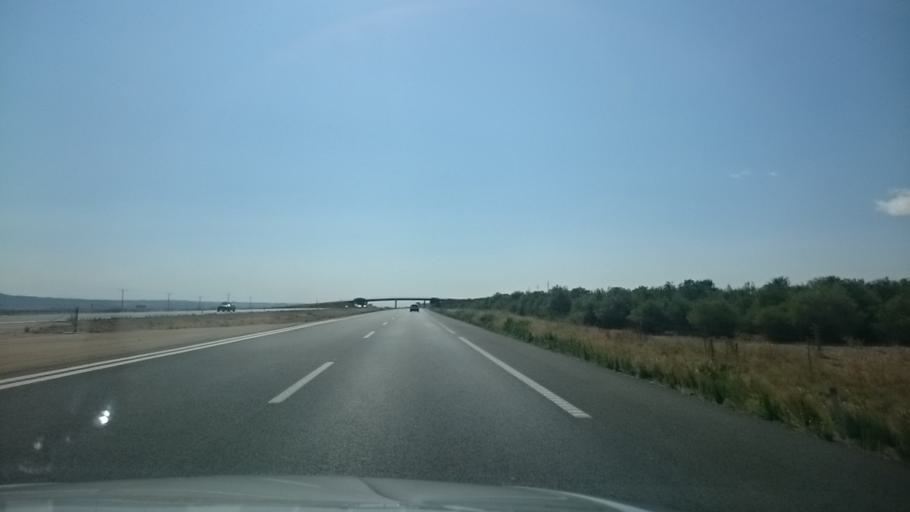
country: ES
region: Aragon
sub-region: Provincia de Zaragoza
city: Gallur
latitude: 41.8418
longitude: -1.3474
